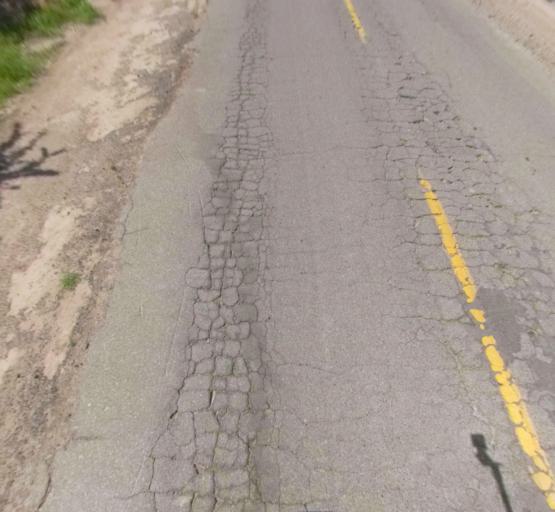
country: US
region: California
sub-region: Madera County
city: Chowchilla
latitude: 37.0501
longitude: -120.3831
